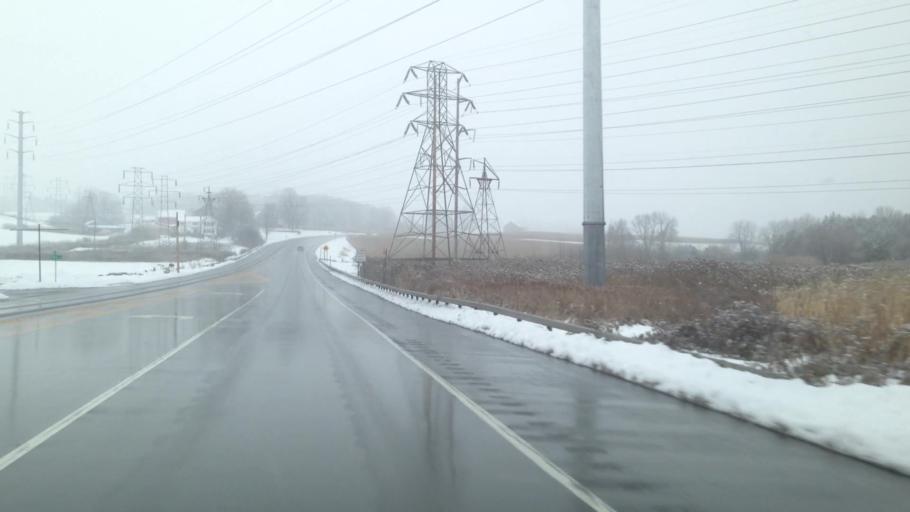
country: US
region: New York
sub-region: Onondaga County
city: Peru
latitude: 43.0376
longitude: -76.4024
